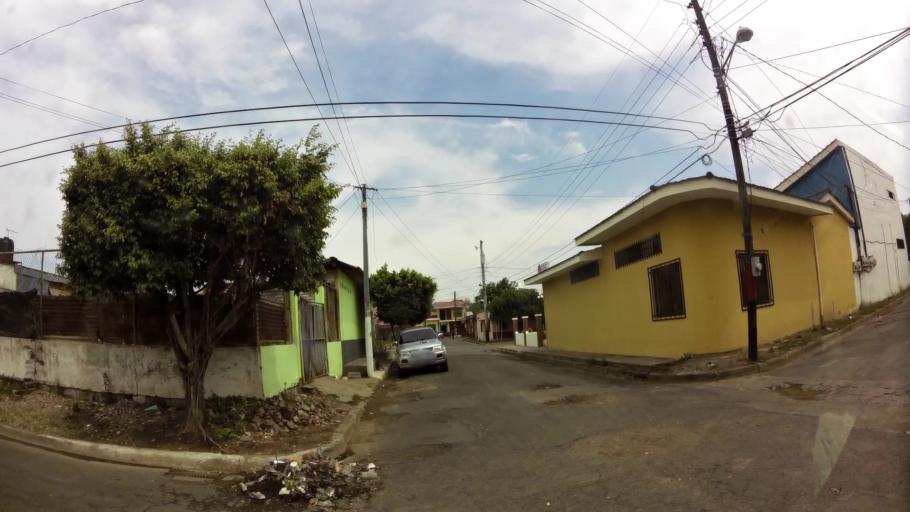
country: NI
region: Rivas
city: Rivas
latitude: 11.4417
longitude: -85.8258
